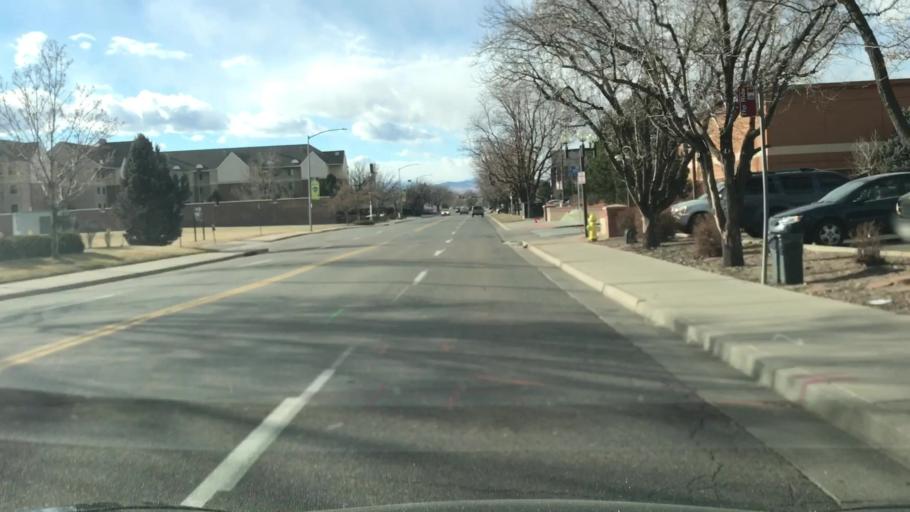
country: US
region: Colorado
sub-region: Arapahoe County
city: Glendale
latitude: 39.7074
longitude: -104.9359
